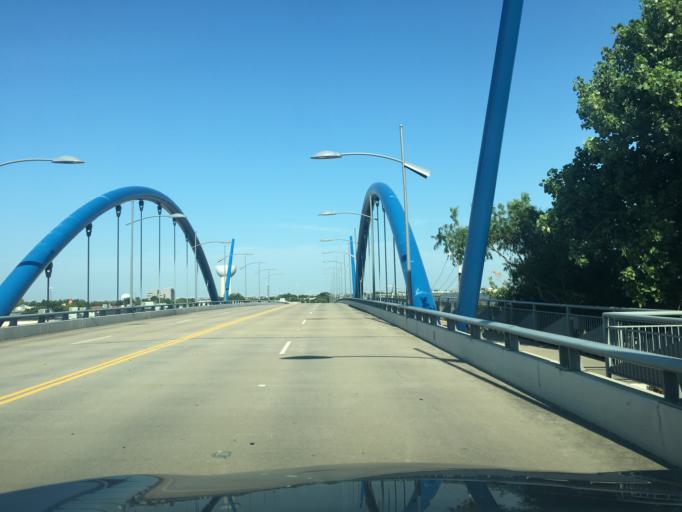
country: US
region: Texas
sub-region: Dallas County
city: Addison
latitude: 32.9563
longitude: -96.8380
